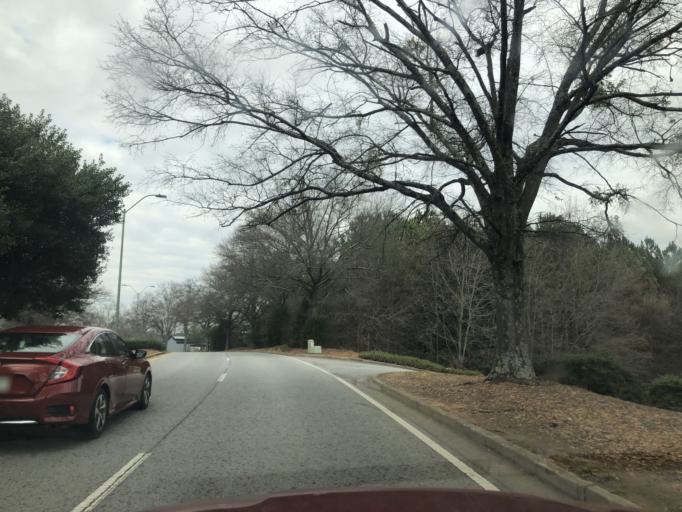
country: US
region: Georgia
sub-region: Clayton County
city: Morrow
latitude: 33.5754
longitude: -84.3456
